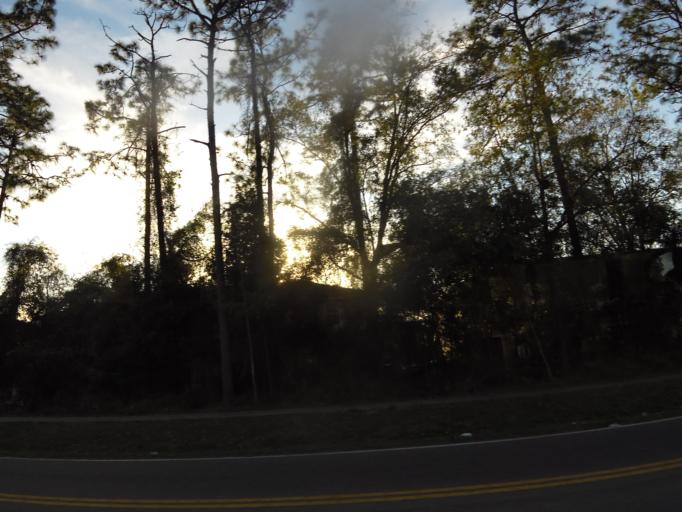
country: US
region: Florida
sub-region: Duval County
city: Jacksonville
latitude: 30.4563
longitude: -81.6693
